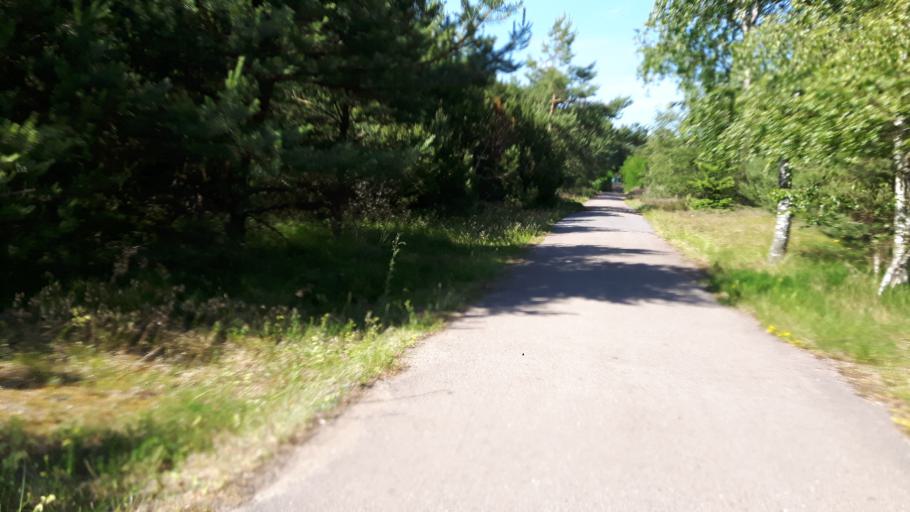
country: LT
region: Klaipedos apskritis
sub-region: Klaipeda
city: Klaipeda
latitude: 55.6917
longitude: 21.1029
